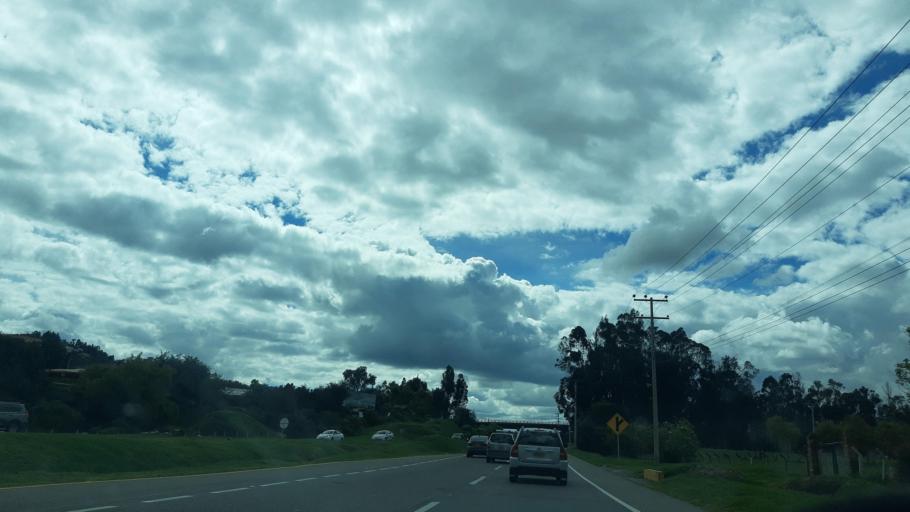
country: CO
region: Cundinamarca
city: Tocancipa
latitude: 4.9701
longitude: -73.8986
